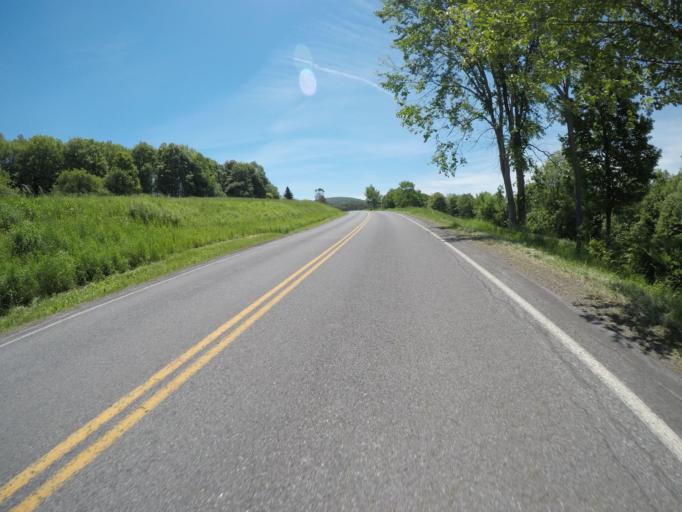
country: US
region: New York
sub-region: Delaware County
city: Delhi
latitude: 42.1864
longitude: -74.8016
